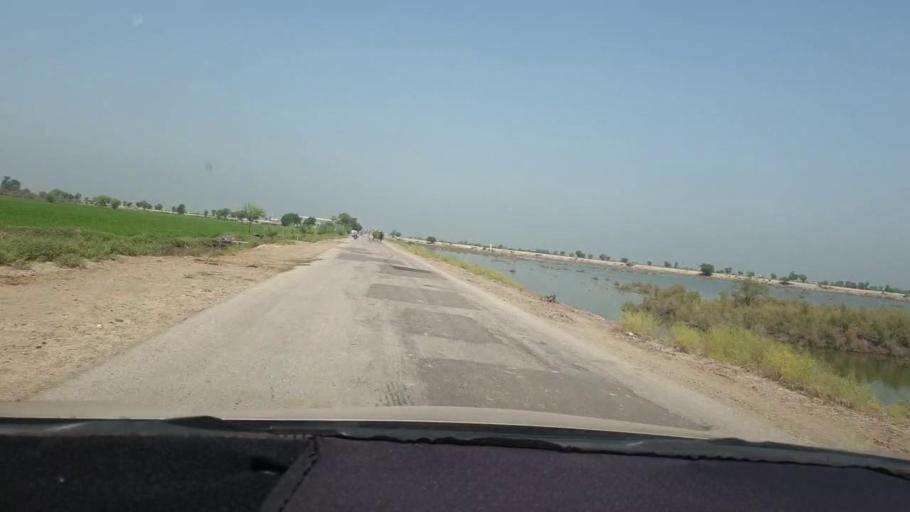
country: PK
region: Sindh
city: Shahdadkot
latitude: 27.8441
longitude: 68.0030
